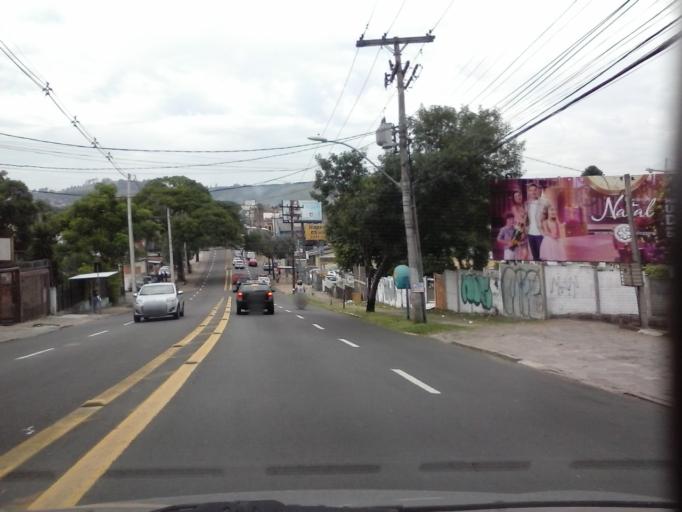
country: BR
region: Rio Grande do Sul
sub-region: Porto Alegre
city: Porto Alegre
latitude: -30.0671
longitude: -51.2058
